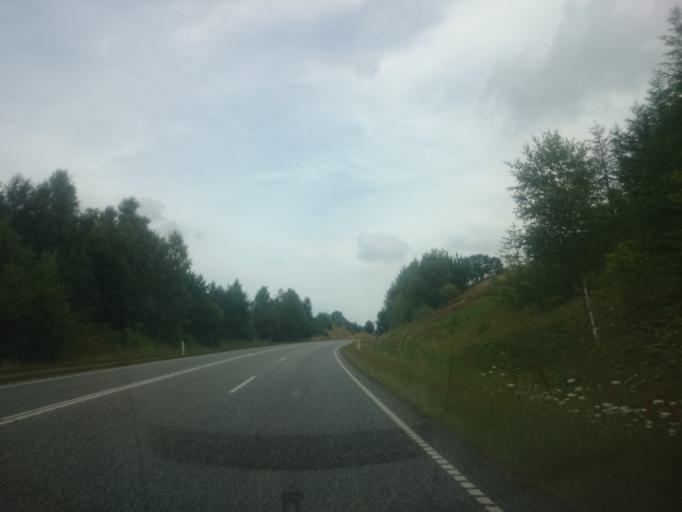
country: DK
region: South Denmark
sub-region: Vejle Kommune
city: Jelling
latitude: 55.6785
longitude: 9.3809
